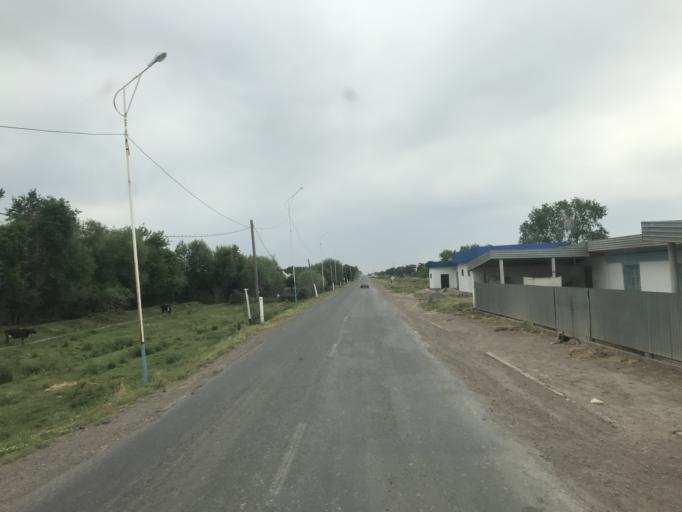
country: KZ
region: Ongtustik Qazaqstan
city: Asykata
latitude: 40.9424
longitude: 68.4154
